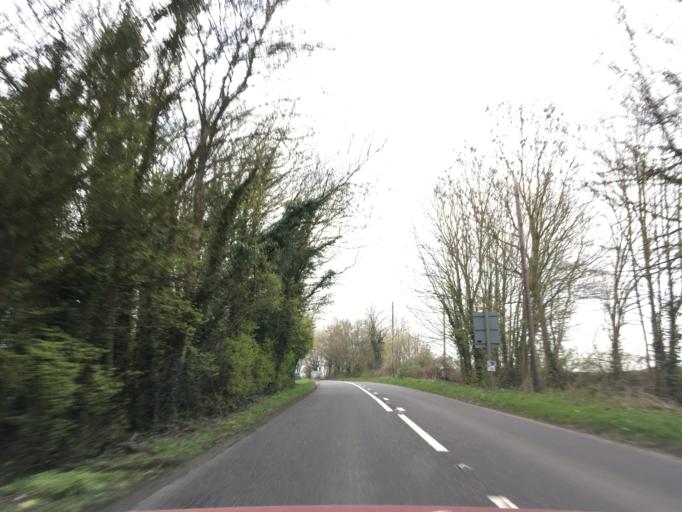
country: GB
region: England
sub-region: Gloucestershire
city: Coates
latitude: 51.6987
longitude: -2.0003
